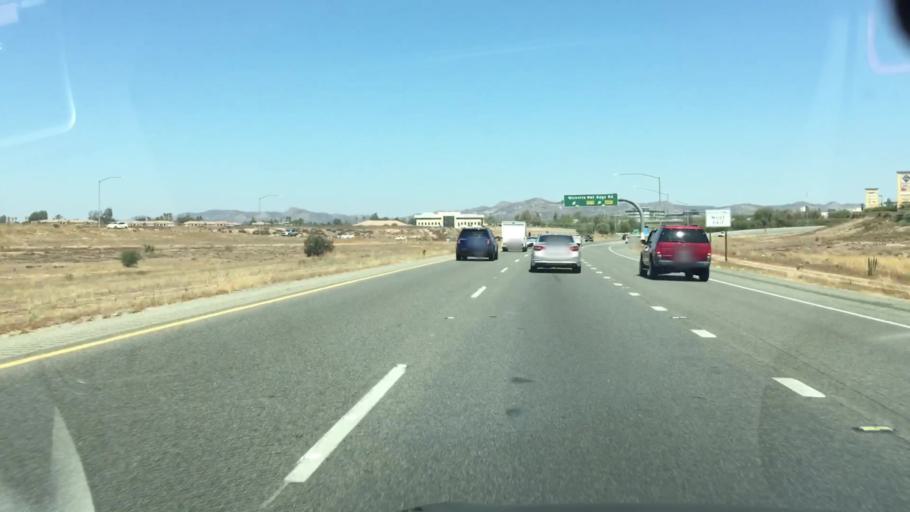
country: US
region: California
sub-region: Riverside County
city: Murrieta Hot Springs
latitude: 33.5502
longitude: -117.1807
